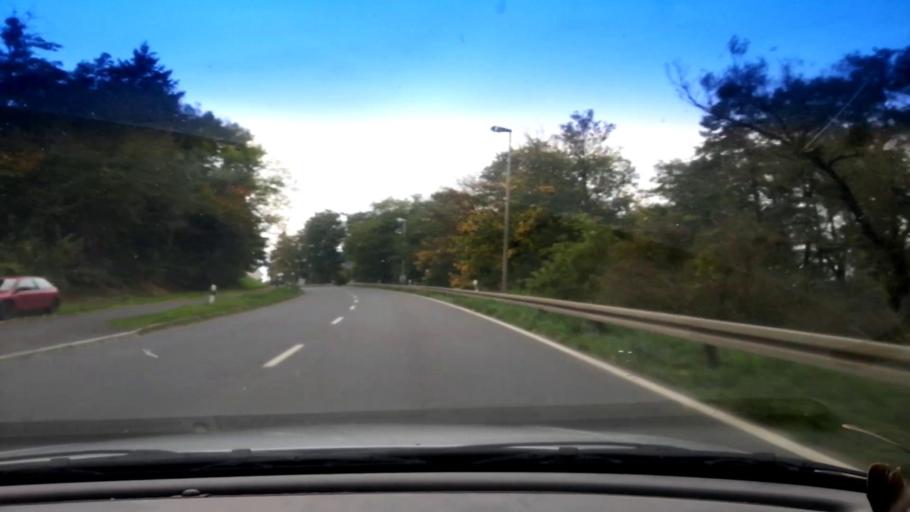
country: DE
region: Bavaria
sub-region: Upper Franconia
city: Baunach
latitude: 49.9833
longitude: 10.8556
